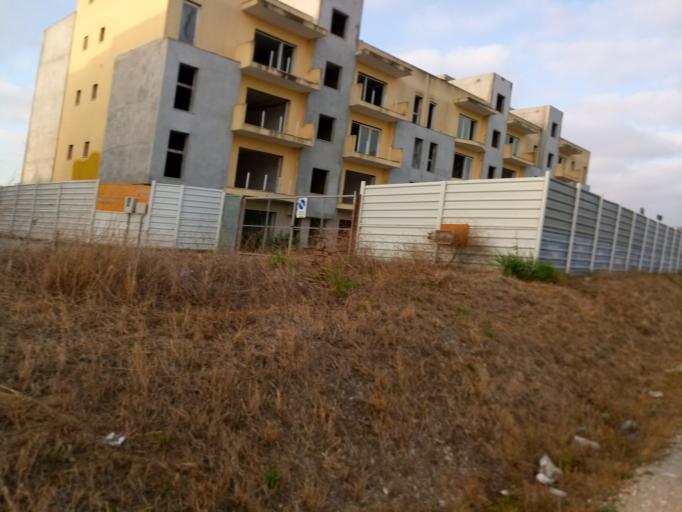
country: PT
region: Leiria
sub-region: Caldas da Rainha
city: Caldas da Rainha
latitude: 39.4162
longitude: -9.1449
